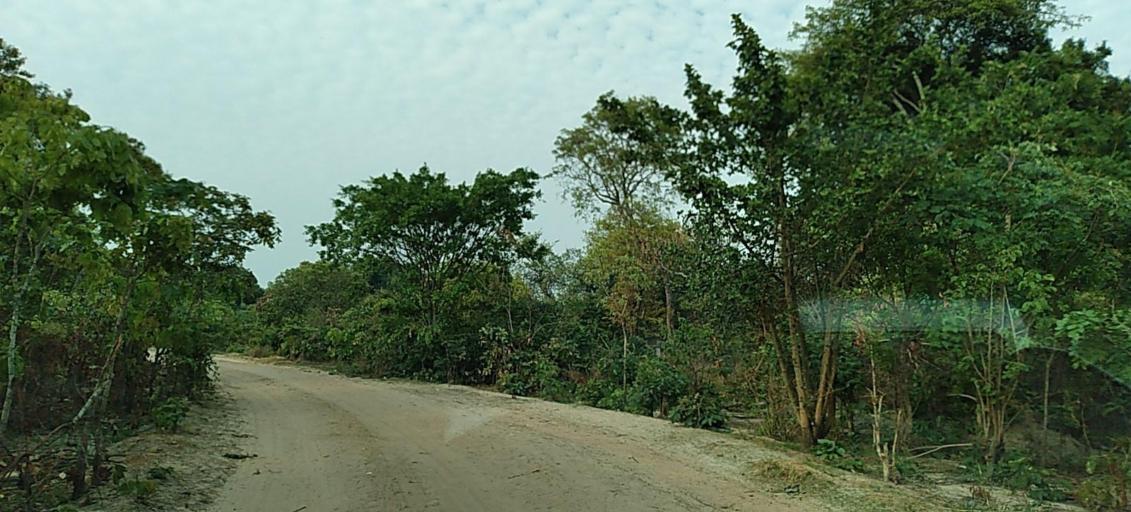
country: ZM
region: Copperbelt
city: Kalulushi
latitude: -12.8966
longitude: 27.6859
